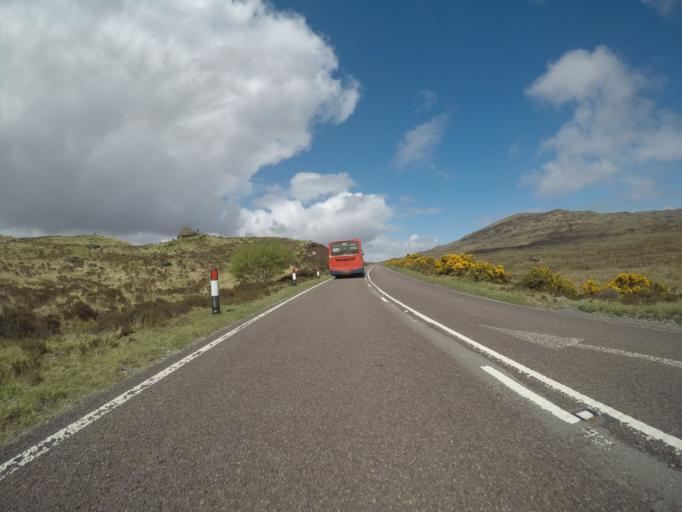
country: GB
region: Scotland
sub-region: Highland
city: Isle of Skye
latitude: 57.2972
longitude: -6.1821
